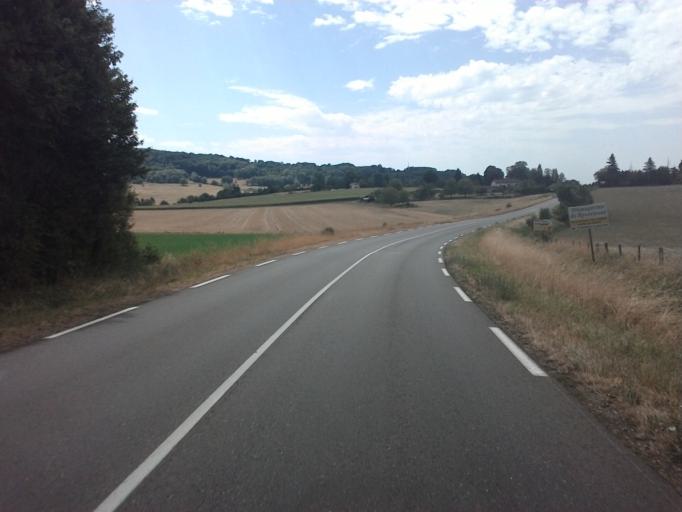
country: FR
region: Franche-Comte
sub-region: Departement du Jura
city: Saint-Amour
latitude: 46.4627
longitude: 5.3574
